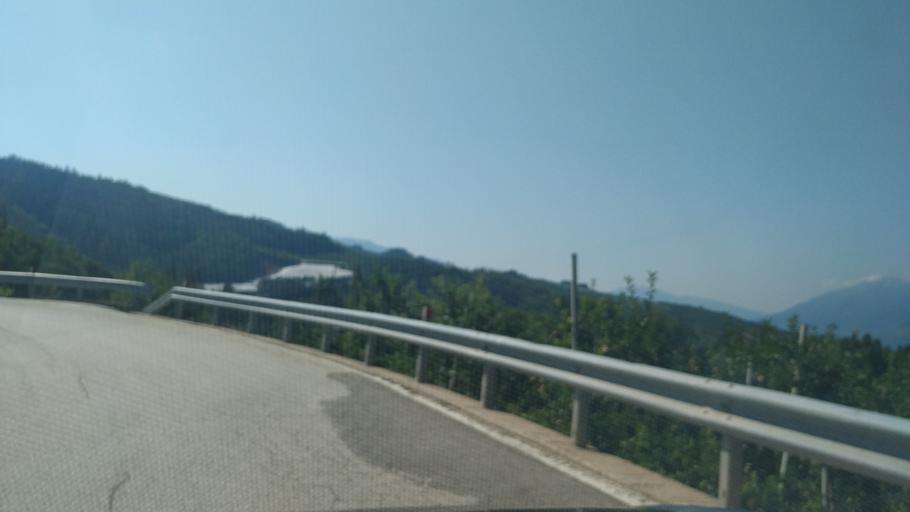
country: IT
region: Trentino-Alto Adige
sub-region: Provincia di Trento
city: Sanzeno
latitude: 46.3726
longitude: 11.0801
